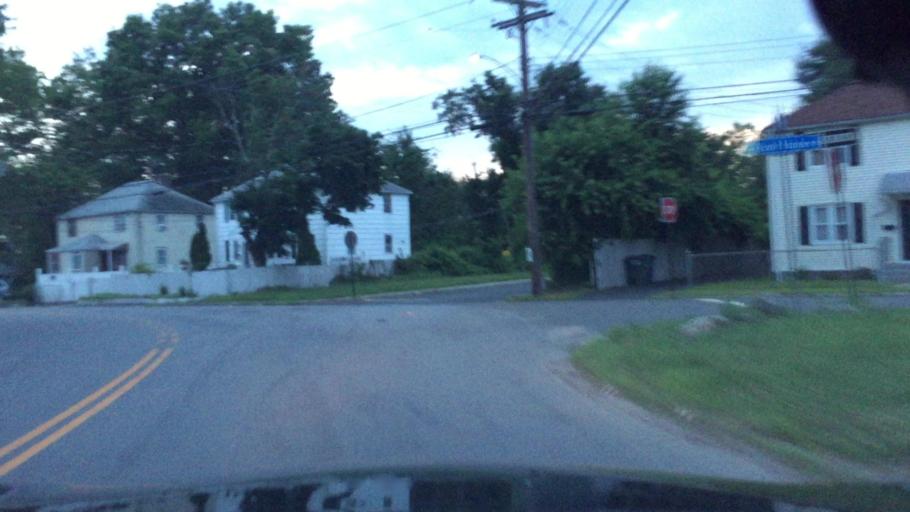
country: US
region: Connecticut
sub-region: Fairfield County
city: Stratford
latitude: 41.2044
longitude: -73.1600
